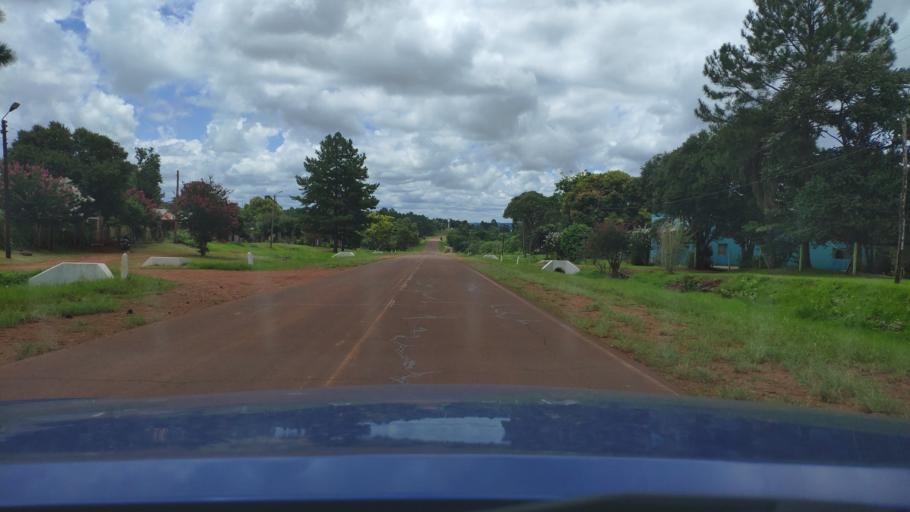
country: AR
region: Misiones
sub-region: Departamento de San Javier
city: San Javier
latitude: -27.8624
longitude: -55.2550
